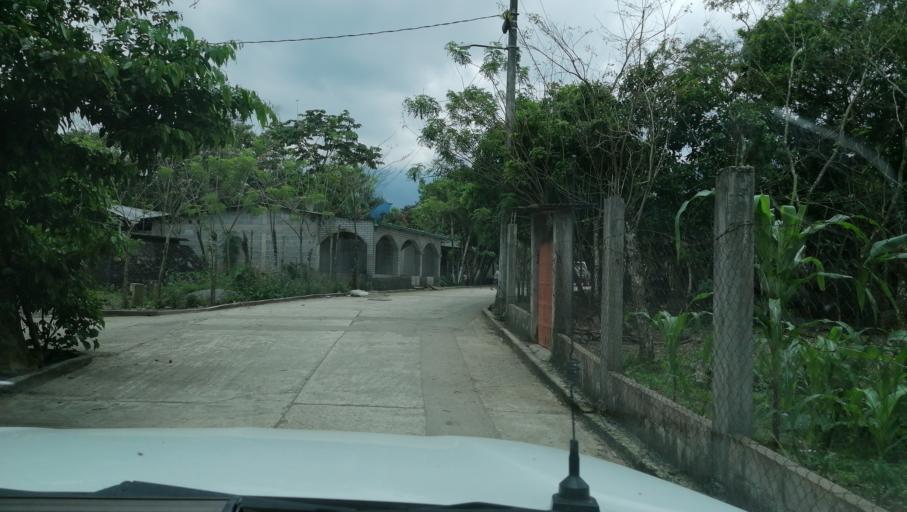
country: MX
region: Chiapas
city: Ocotepec
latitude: 17.2873
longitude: -93.2208
